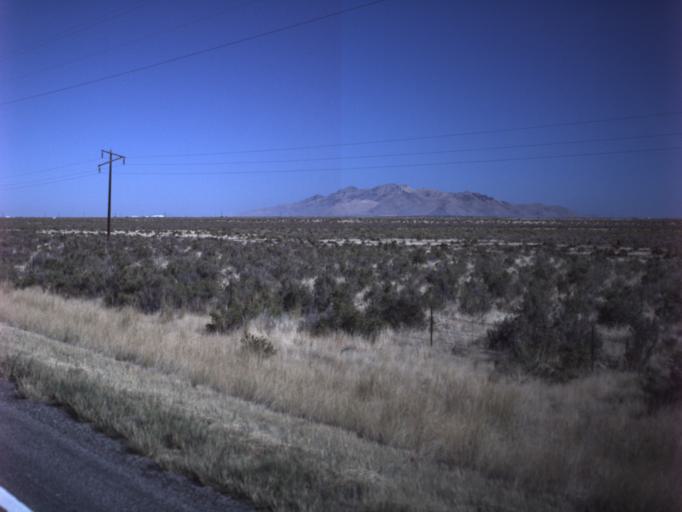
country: US
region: Utah
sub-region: Tooele County
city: Grantsville
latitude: 40.6666
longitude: -112.5437
